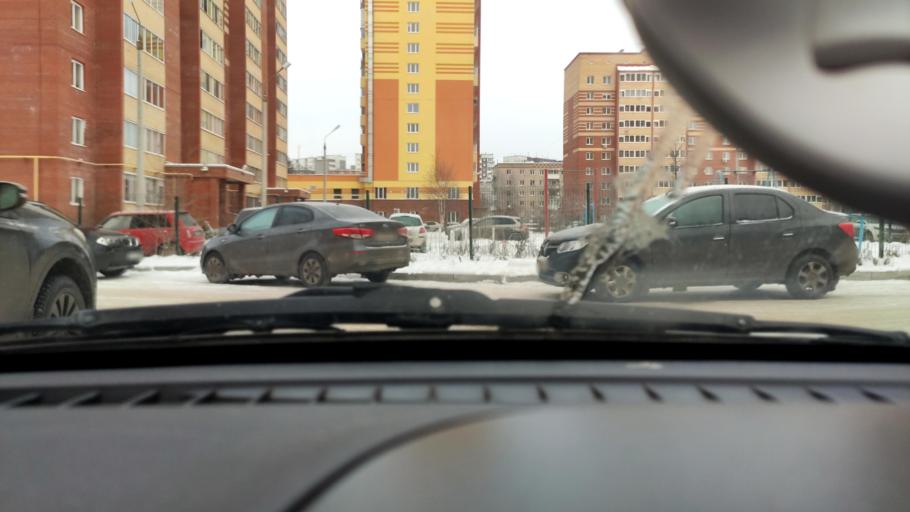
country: RU
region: Perm
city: Perm
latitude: 58.0832
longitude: 56.4047
